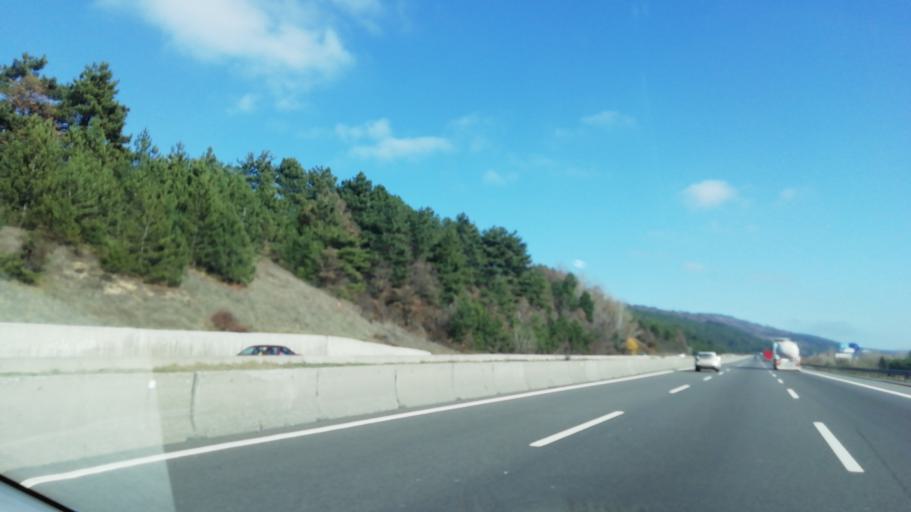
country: TR
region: Bolu
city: Bolu
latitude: 40.7350
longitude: 31.8128
